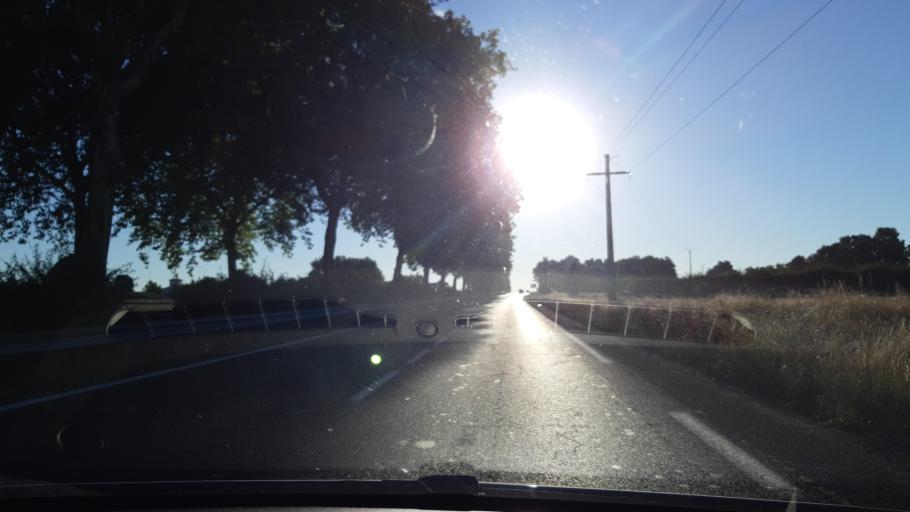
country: FR
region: Poitou-Charentes
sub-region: Departement des Deux-Sevres
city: Chauray
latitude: 46.3488
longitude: -0.3483
